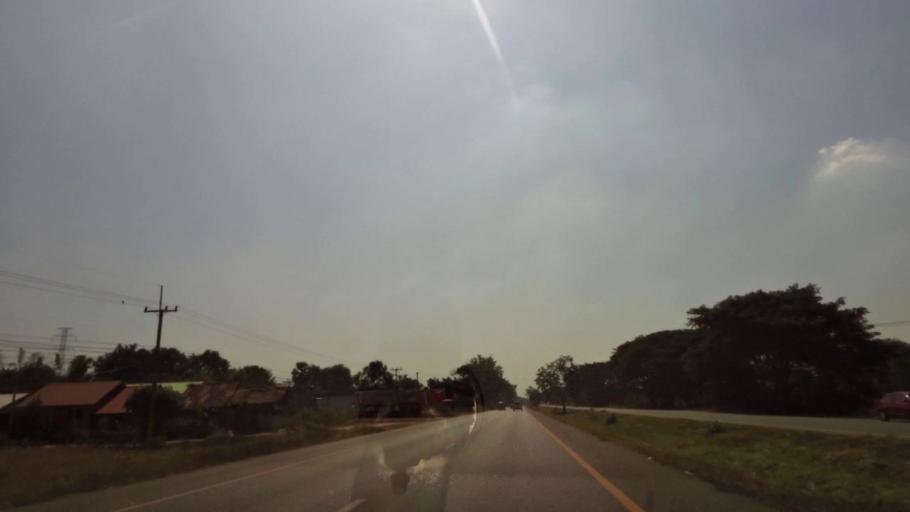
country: TH
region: Phichit
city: Wachira Barami
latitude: 16.3879
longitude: 100.1380
